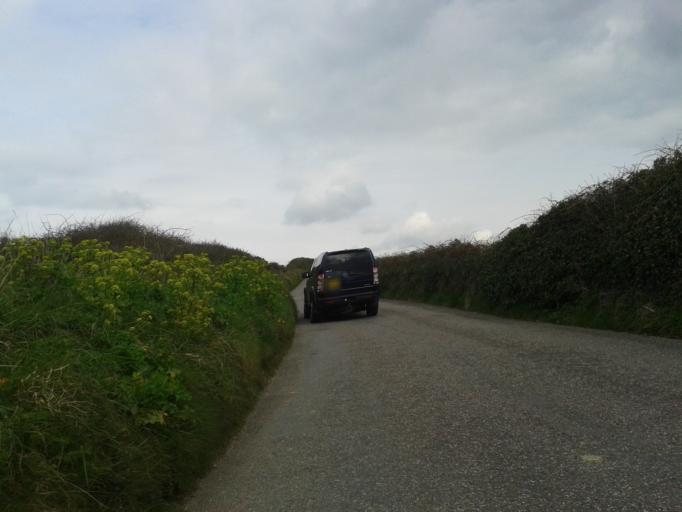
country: GB
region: England
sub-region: Devon
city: Braunton
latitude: 51.1854
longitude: -4.2025
